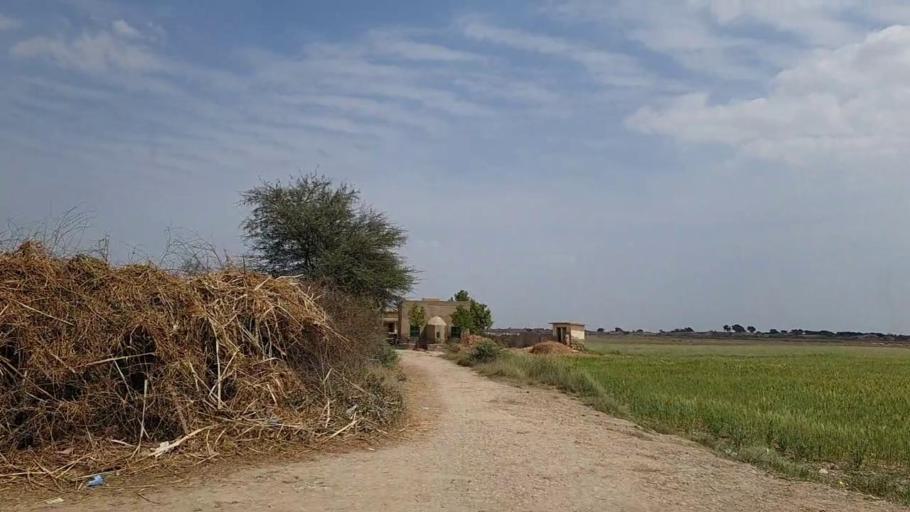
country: PK
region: Sindh
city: Daro Mehar
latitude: 24.8416
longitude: 68.1992
